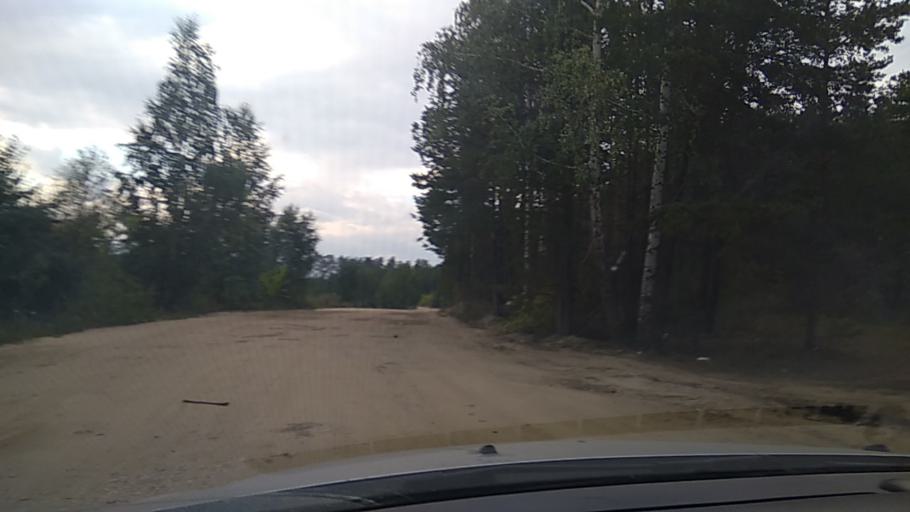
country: RU
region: Chelyabinsk
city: Kyshtym
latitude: 55.6813
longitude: 60.5730
